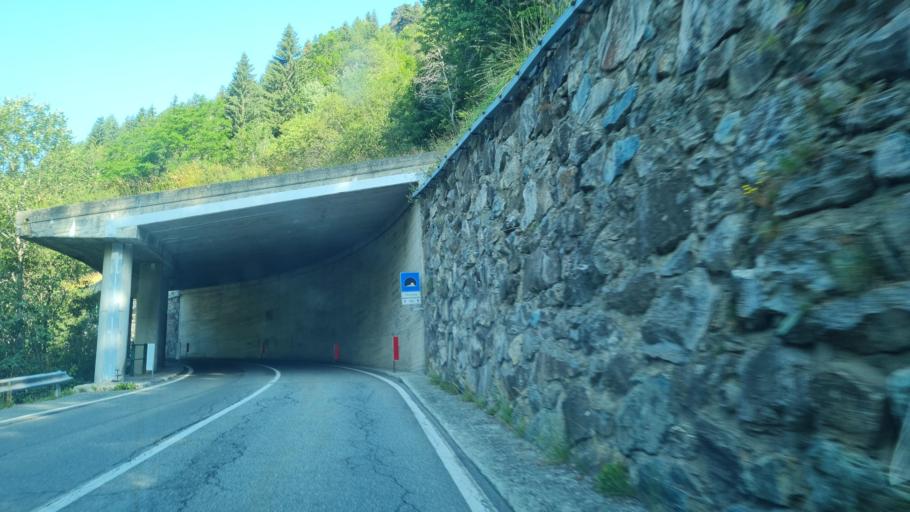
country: IT
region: Aosta Valley
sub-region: Valle d'Aosta
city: Champorcher
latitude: 45.6244
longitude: 7.6270
